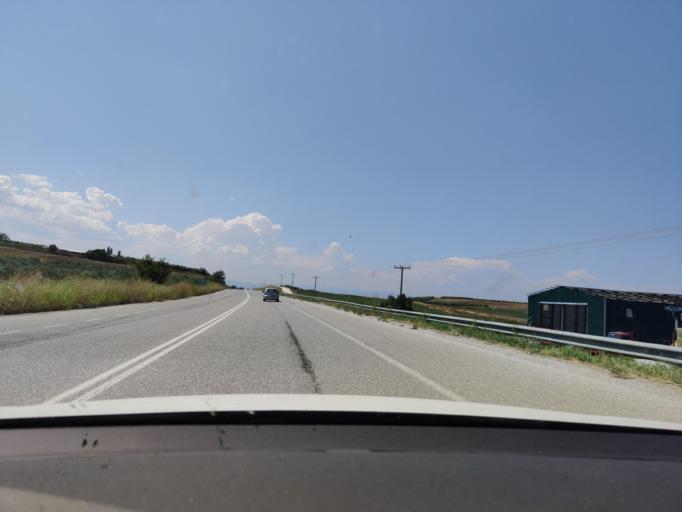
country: GR
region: Central Macedonia
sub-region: Nomos Serron
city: Draviskos
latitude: 40.9327
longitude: 23.8667
